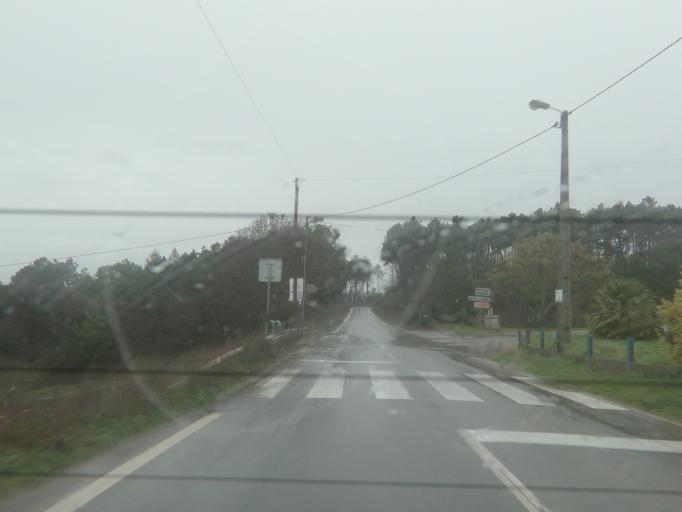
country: PT
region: Vila Real
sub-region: Sabrosa
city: Vilela
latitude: 41.2258
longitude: -7.6777
